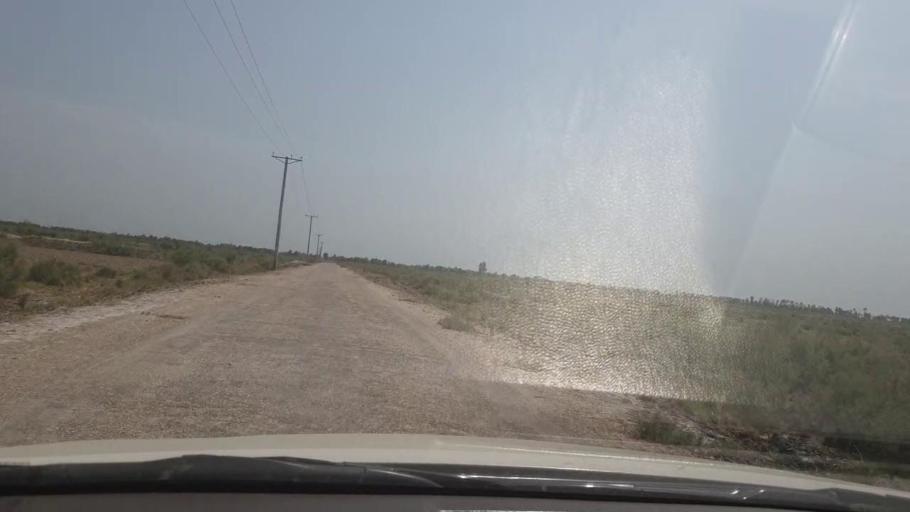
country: PK
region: Sindh
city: Garhi Yasin
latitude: 27.9855
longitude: 68.5021
